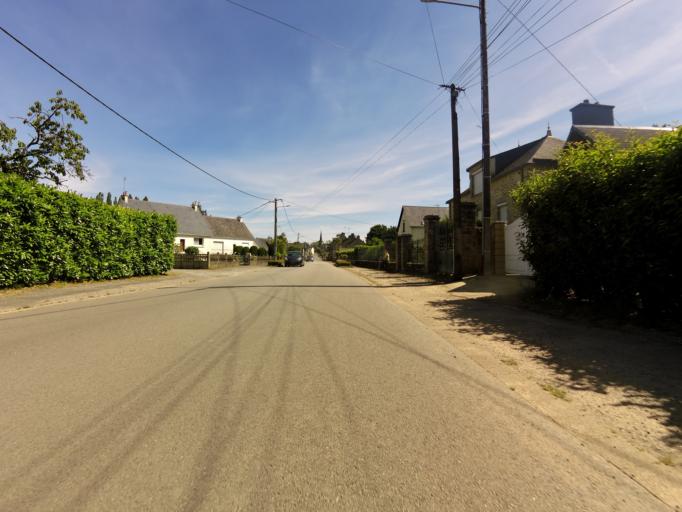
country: FR
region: Brittany
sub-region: Departement du Morbihan
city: Malansac
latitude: 47.6812
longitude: -2.3006
